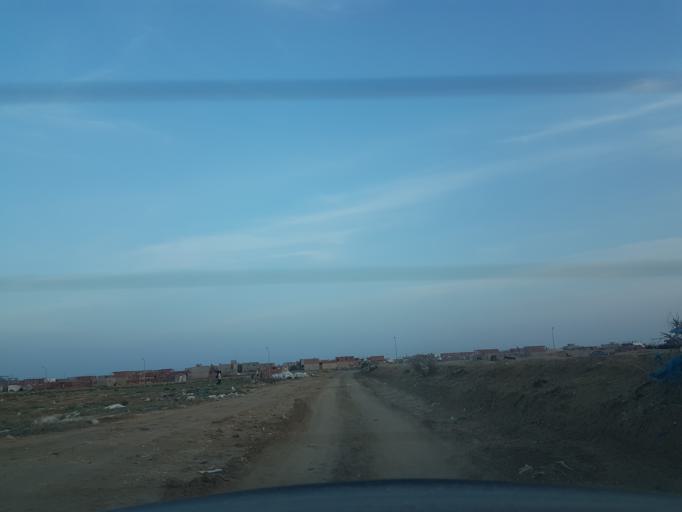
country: TN
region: Safaqis
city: Sfax
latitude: 34.7028
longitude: 10.6974
